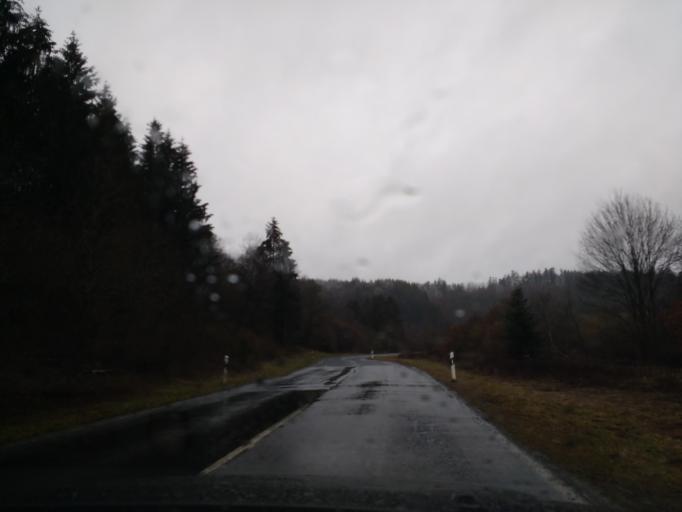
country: DE
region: Rheinland-Pfalz
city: Malborn
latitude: 49.7254
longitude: 6.9754
